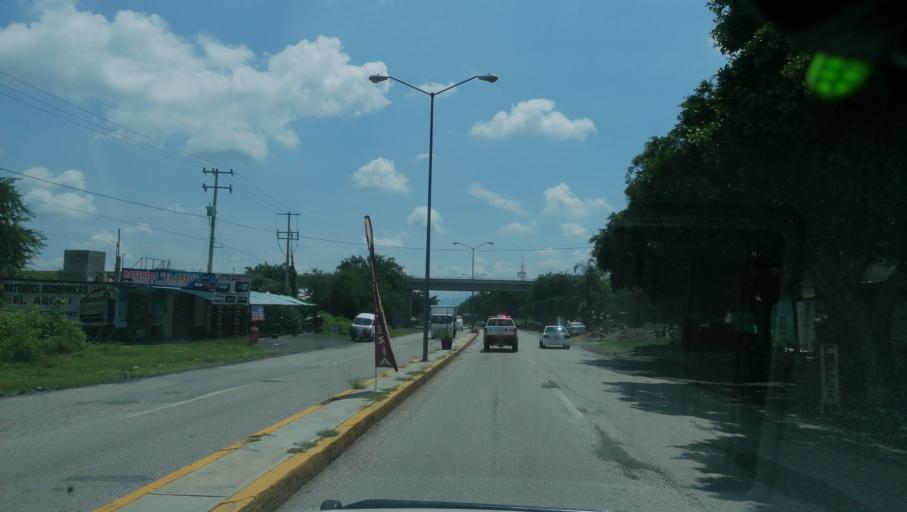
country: MX
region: Morelos
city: Amayuca
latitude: 18.7075
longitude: -98.7996
